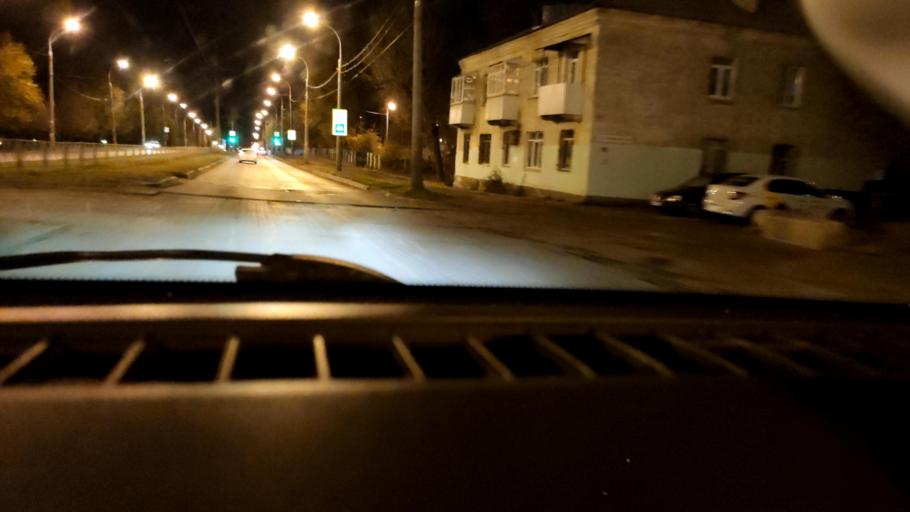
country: RU
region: Samara
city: Samara
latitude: 53.2048
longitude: 50.2136
